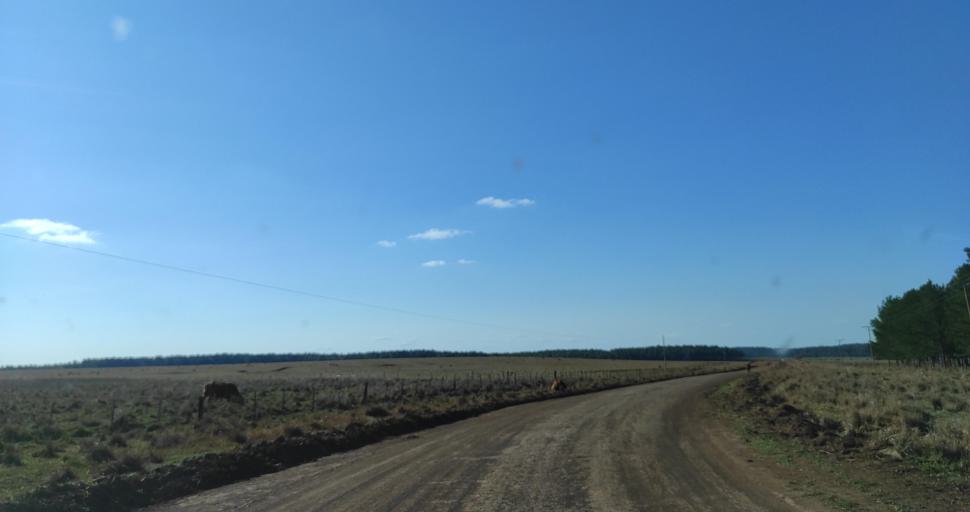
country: PY
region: Itapua
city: San Juan del Parana
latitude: -27.4337
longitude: -56.0851
